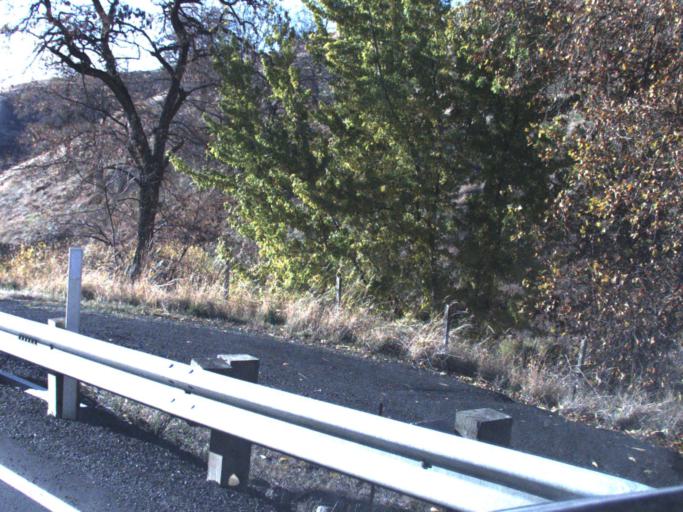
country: US
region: Washington
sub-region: Whitman County
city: Colfax
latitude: 46.7292
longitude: -117.4882
